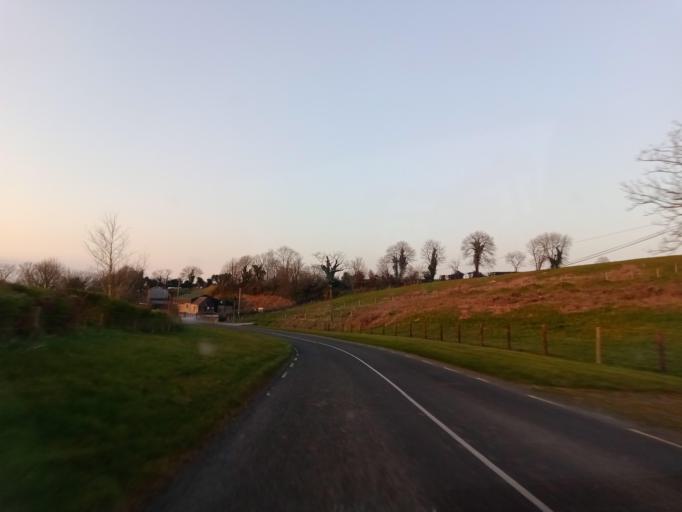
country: IE
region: Leinster
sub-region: Laois
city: Abbeyleix
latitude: 52.8936
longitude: -7.3144
